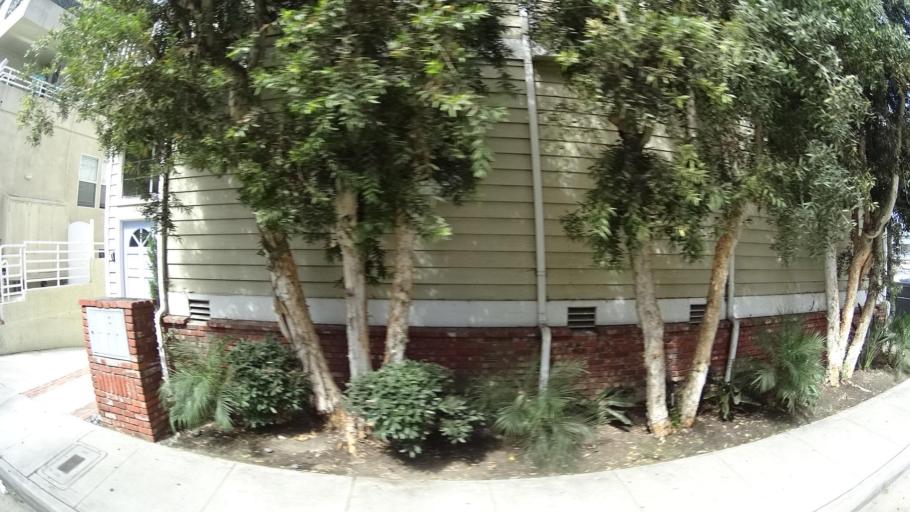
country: US
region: California
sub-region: Los Angeles County
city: Hermosa Beach
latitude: 33.8630
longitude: -118.3950
